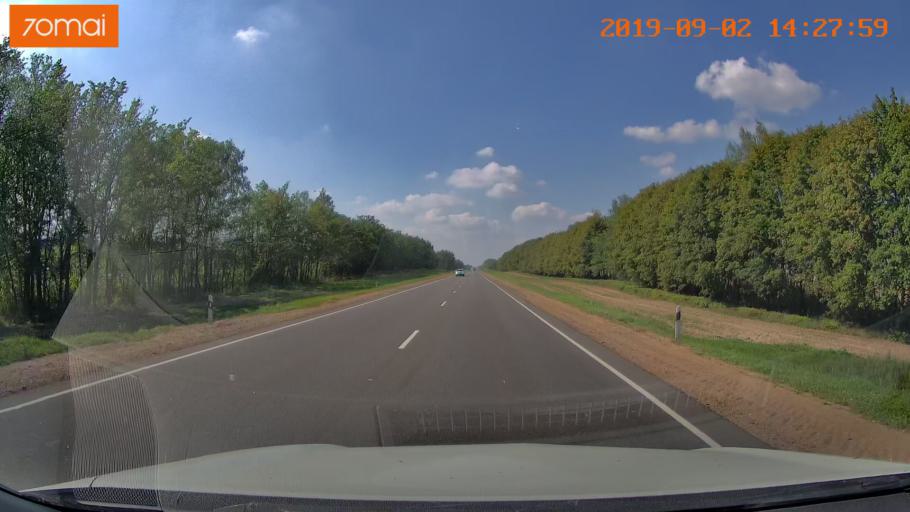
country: BY
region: Mogilev
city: Ramanavichy
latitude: 53.8516
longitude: 30.5558
